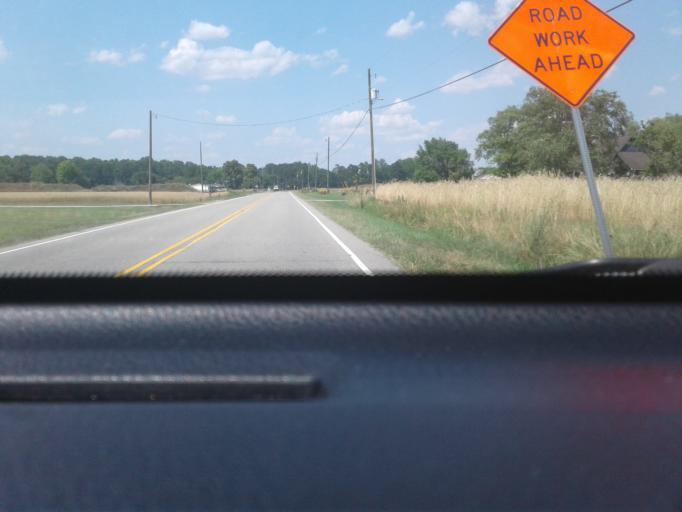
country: US
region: North Carolina
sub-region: Cumberland County
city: Eastover
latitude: 35.1380
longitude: -78.7445
